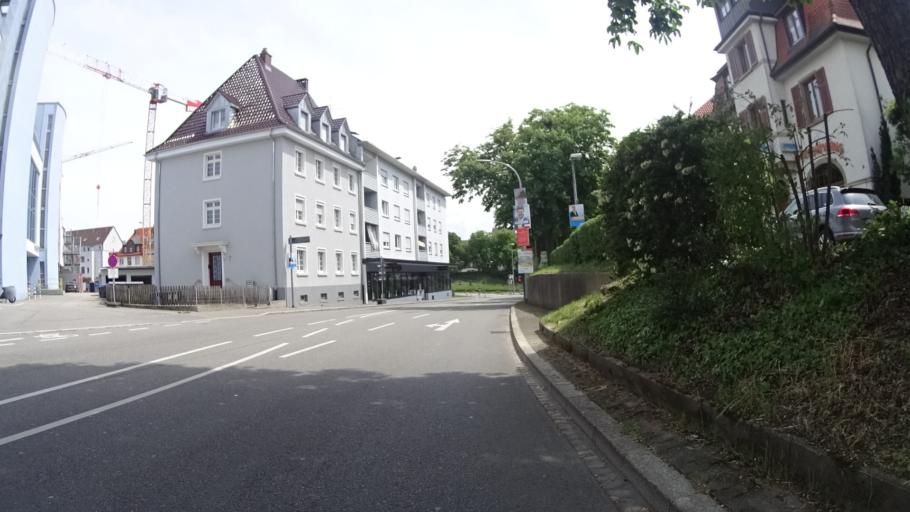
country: DE
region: Baden-Wuerttemberg
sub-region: Freiburg Region
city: Rheinfelden (Baden)
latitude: 47.5586
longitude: 7.7854
